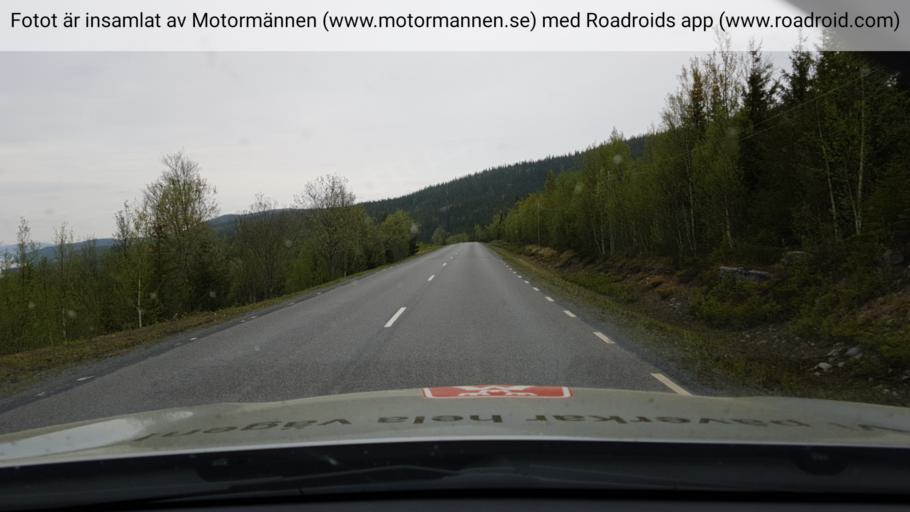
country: SE
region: Jaemtland
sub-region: Are Kommun
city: Are
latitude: 63.4899
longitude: 13.1845
